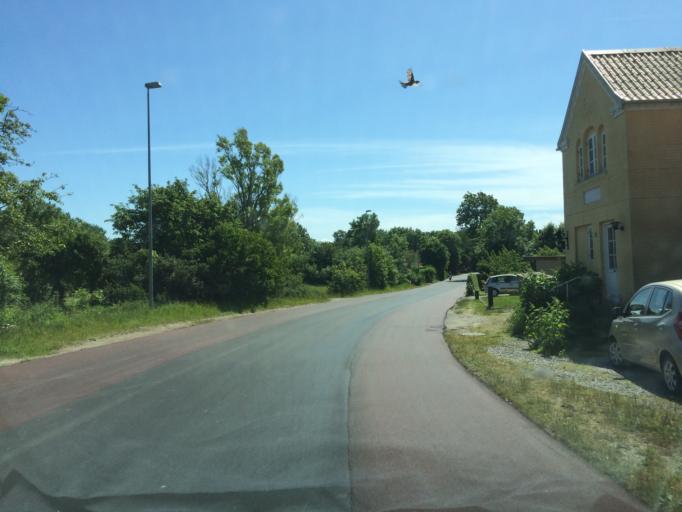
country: DK
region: Central Jutland
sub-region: Samso Kommune
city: Tranebjerg
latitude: 55.8185
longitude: 10.6055
